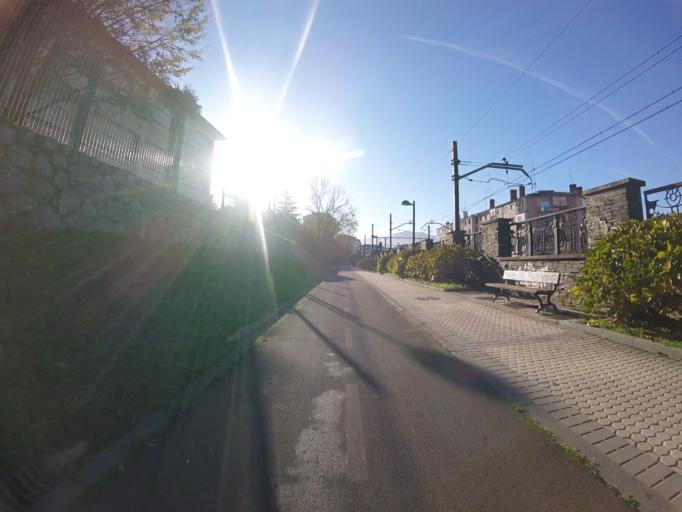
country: ES
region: Basque Country
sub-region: Provincia de Guipuzcoa
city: Lasarte
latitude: 43.2721
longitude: -2.0206
